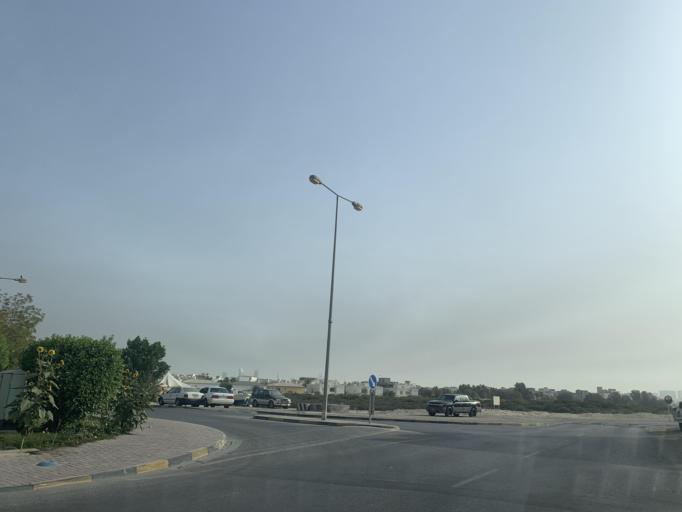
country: BH
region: Northern
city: Madinat `Isa
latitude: 26.1946
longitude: 50.5596
